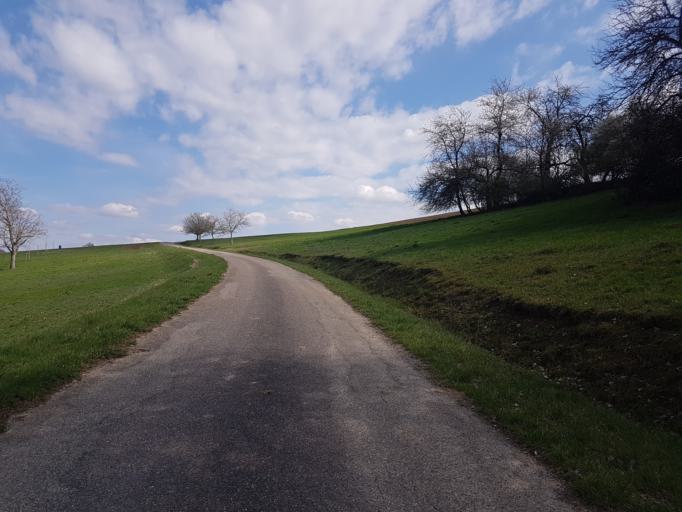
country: DE
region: Baden-Wuerttemberg
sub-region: Regierungsbezirk Stuttgart
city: Weissbach
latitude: 49.3392
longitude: 9.6072
